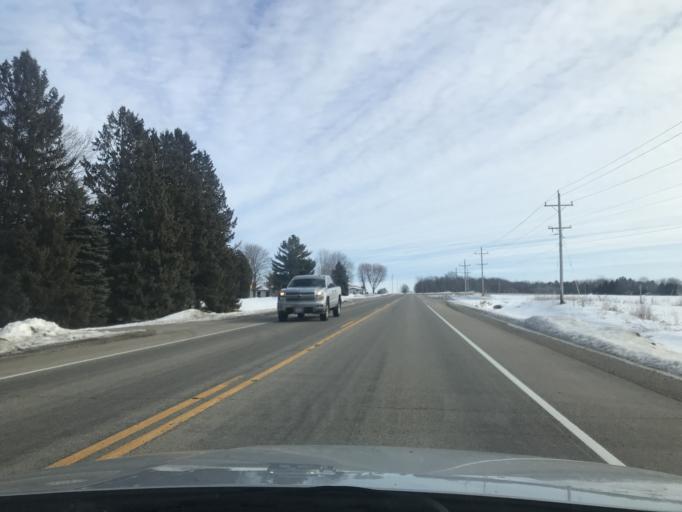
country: US
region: Wisconsin
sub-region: Oconto County
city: Oconto Falls
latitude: 44.8945
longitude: -88.1775
